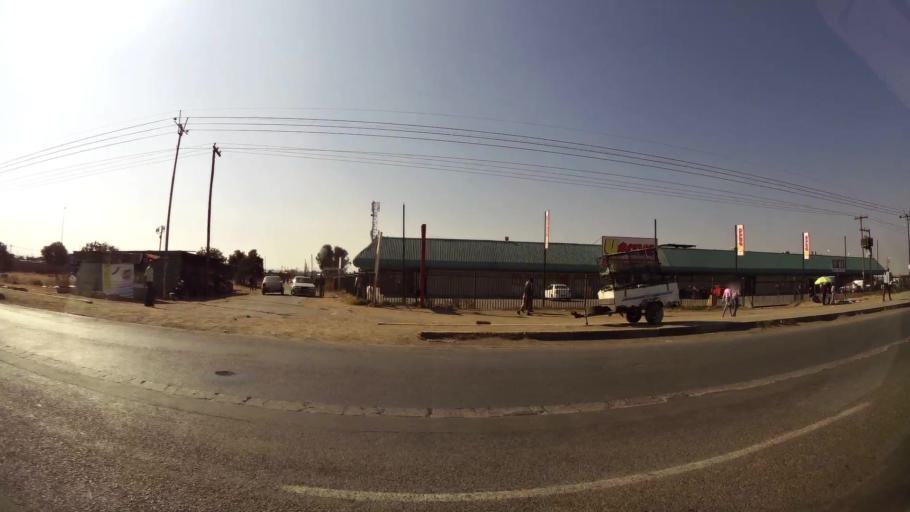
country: ZA
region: Orange Free State
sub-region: Mangaung Metropolitan Municipality
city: Bloemfontein
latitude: -29.1727
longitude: 26.2626
